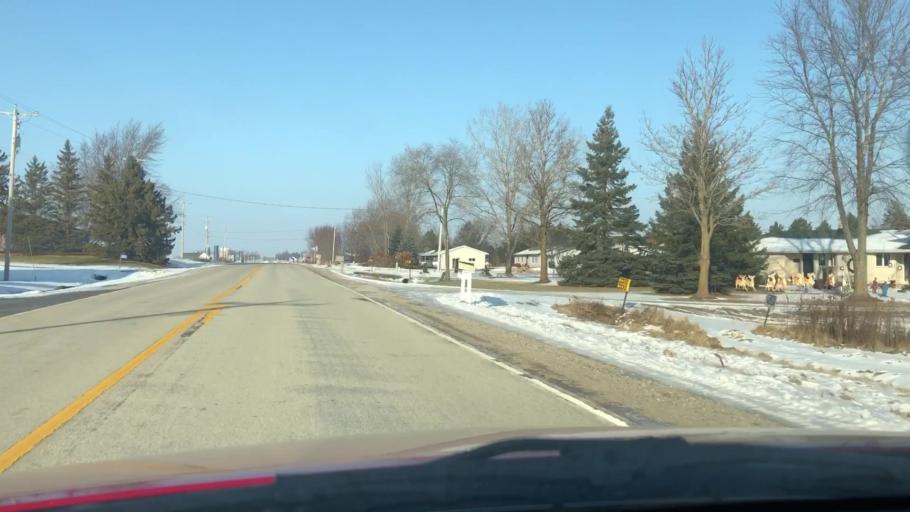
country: US
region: Wisconsin
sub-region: Outagamie County
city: Black Creek
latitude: 44.3986
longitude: -88.3745
